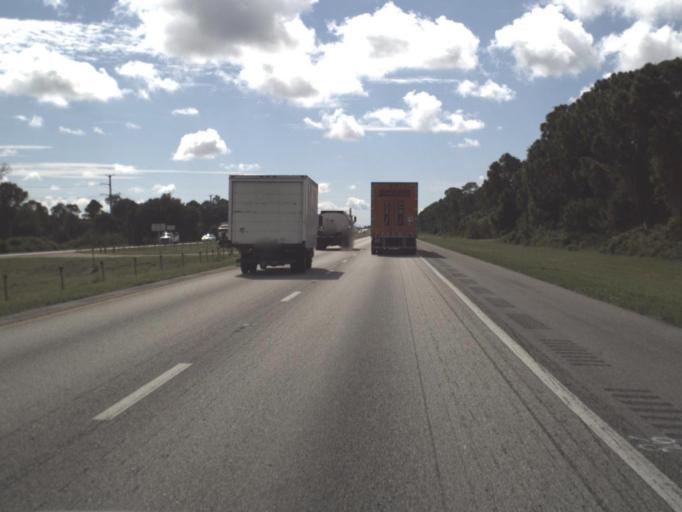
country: US
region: Florida
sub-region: Charlotte County
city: Port Charlotte
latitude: 27.0696
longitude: -82.0960
